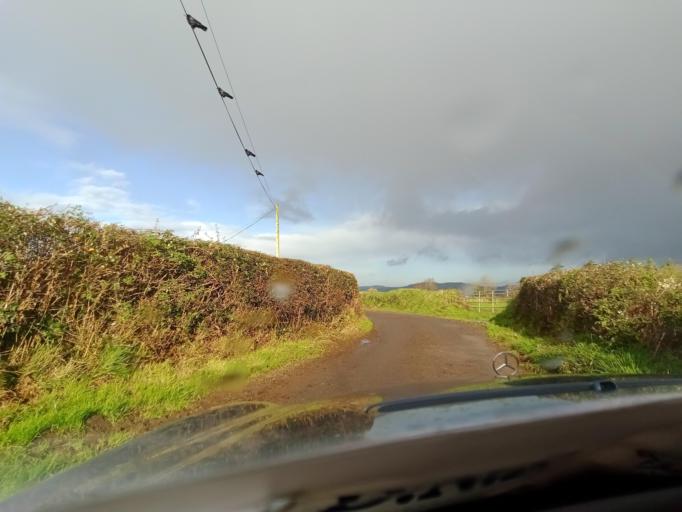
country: IE
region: Leinster
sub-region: Kilkenny
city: Mooncoin
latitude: 52.2933
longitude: -7.2675
